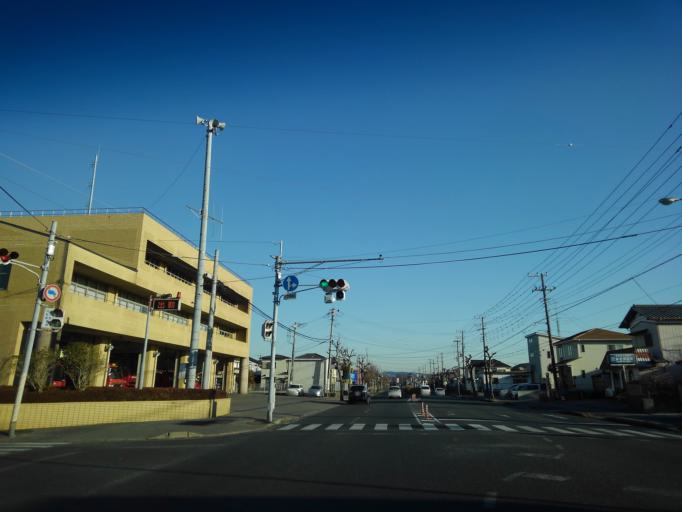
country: JP
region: Chiba
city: Kimitsu
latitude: 35.3215
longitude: 139.9129
